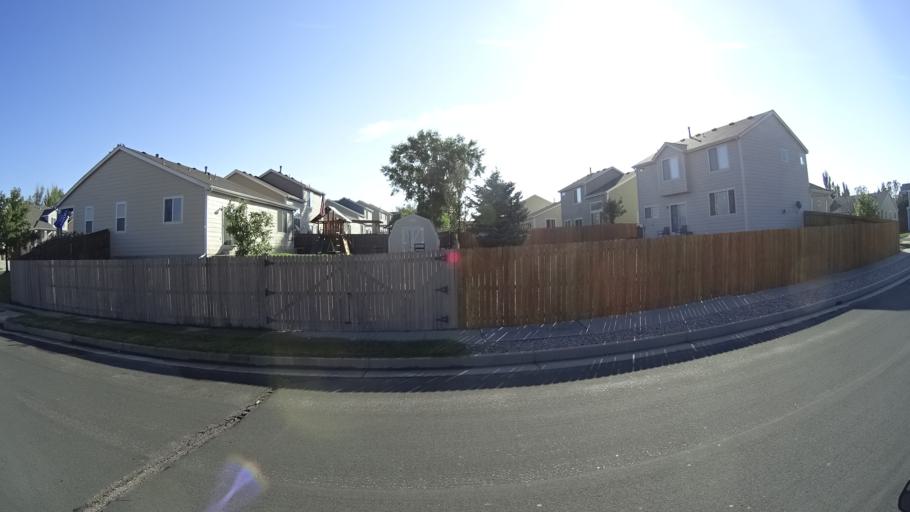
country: US
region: Colorado
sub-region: El Paso County
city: Cimarron Hills
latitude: 38.8848
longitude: -104.6956
